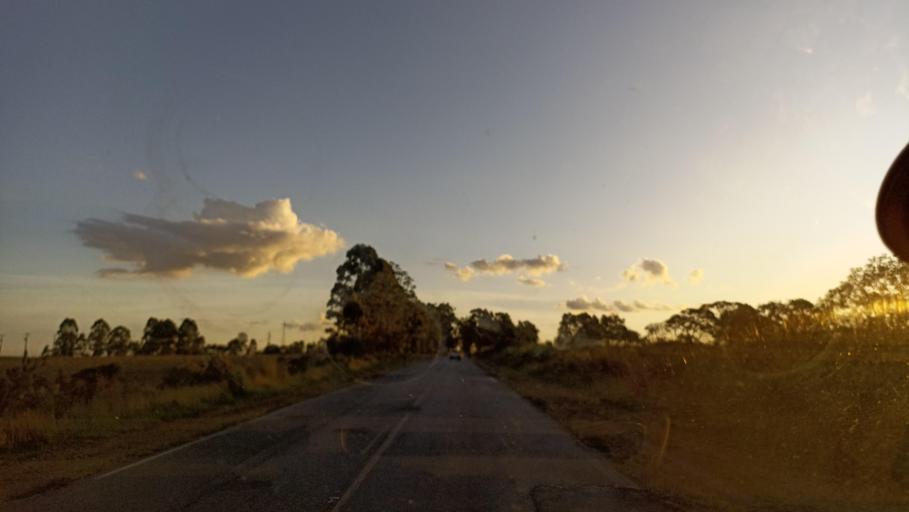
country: BR
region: Minas Gerais
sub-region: Sao Joao Del Rei
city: Sao Joao del Rei
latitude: -21.2385
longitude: -44.3982
